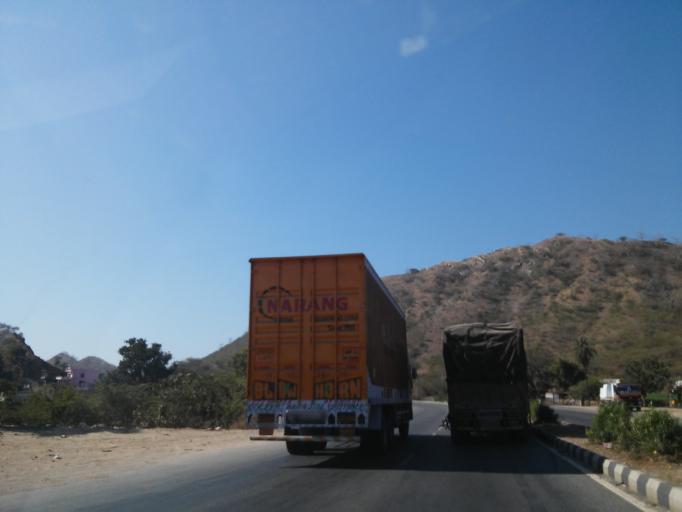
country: IN
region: Rajasthan
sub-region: Udaipur
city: Salumbar
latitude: 24.1937
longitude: 73.7011
